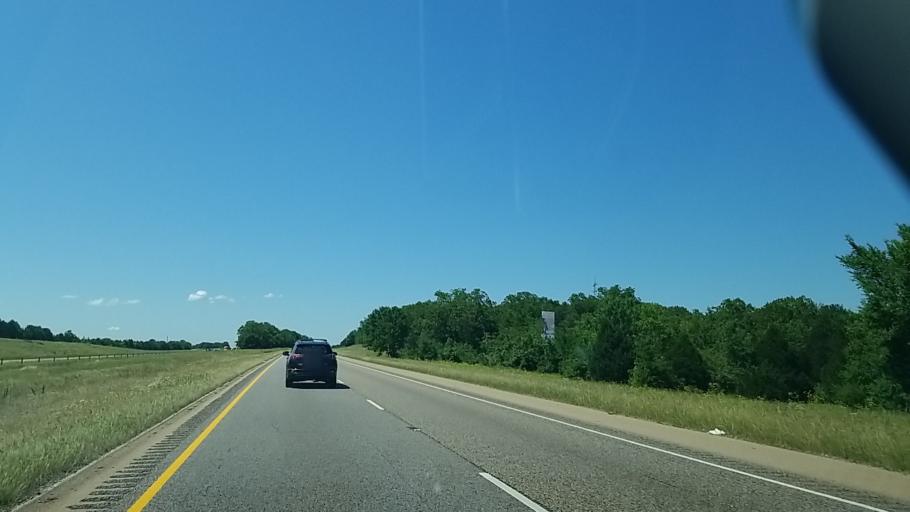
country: US
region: Texas
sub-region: Leon County
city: Buffalo
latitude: 31.5413
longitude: -96.1233
